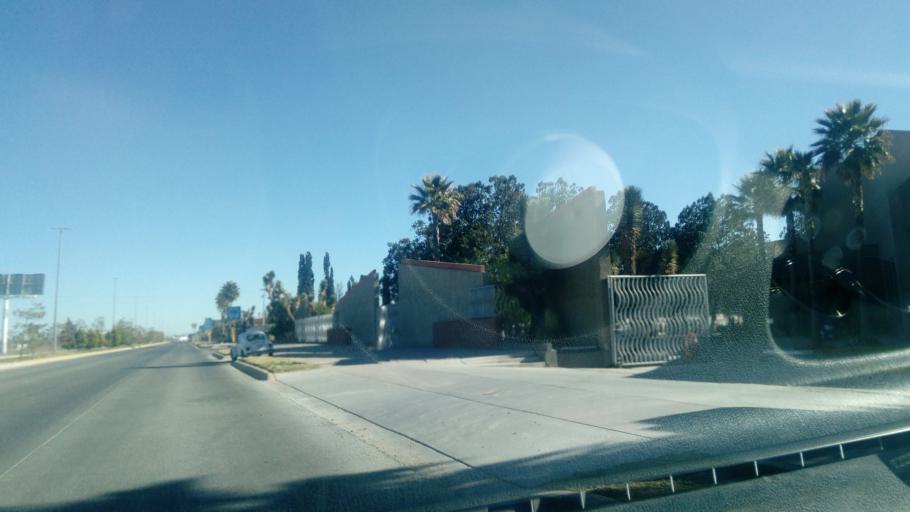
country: MX
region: Durango
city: Victoria de Durango
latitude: 24.0810
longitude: -104.5873
